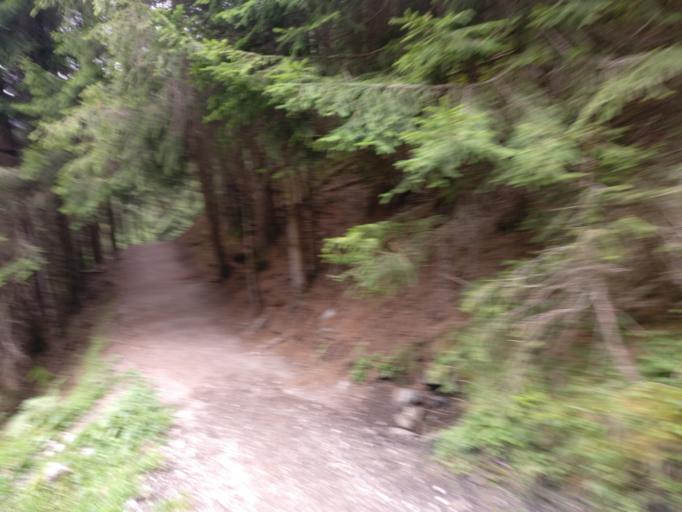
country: AT
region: Tyrol
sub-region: Politischer Bezirk Innsbruck Land
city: Fulpmes
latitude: 47.1474
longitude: 11.3294
